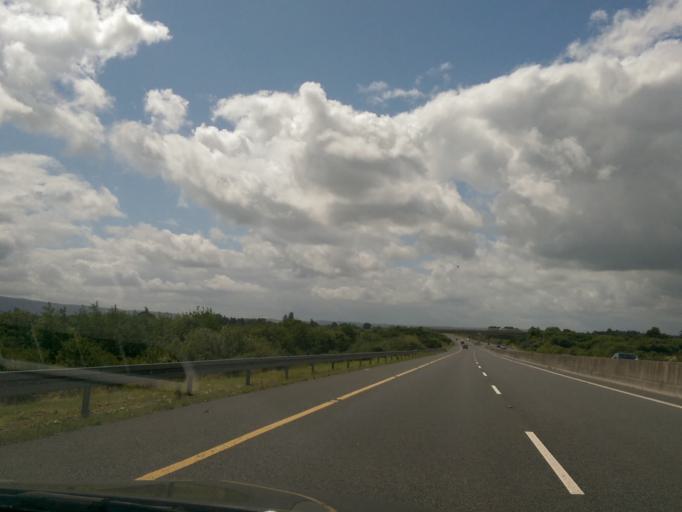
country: IE
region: Munster
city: Cahir
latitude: 52.3416
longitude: -8.0179
